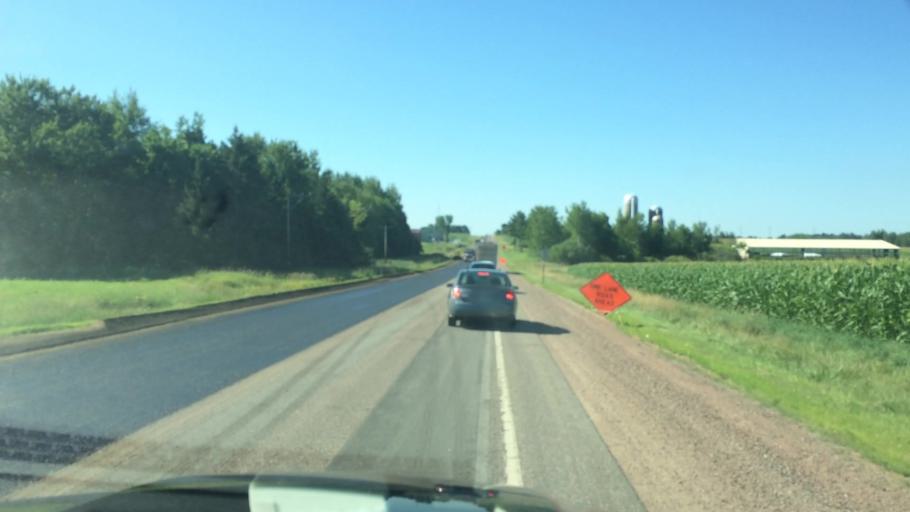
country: US
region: Wisconsin
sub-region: Marathon County
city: Stratford
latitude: 44.8973
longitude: -90.0788
